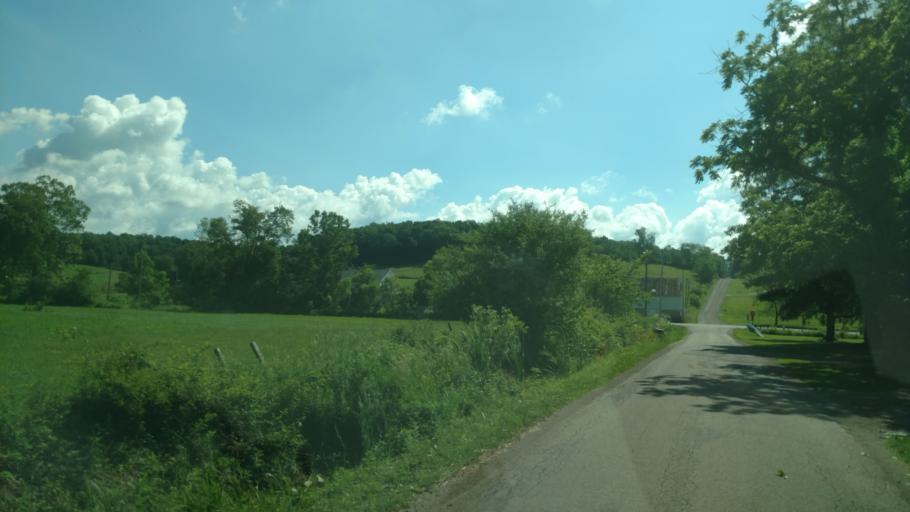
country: US
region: Ohio
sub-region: Knox County
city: Danville
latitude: 40.5015
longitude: -82.2880
